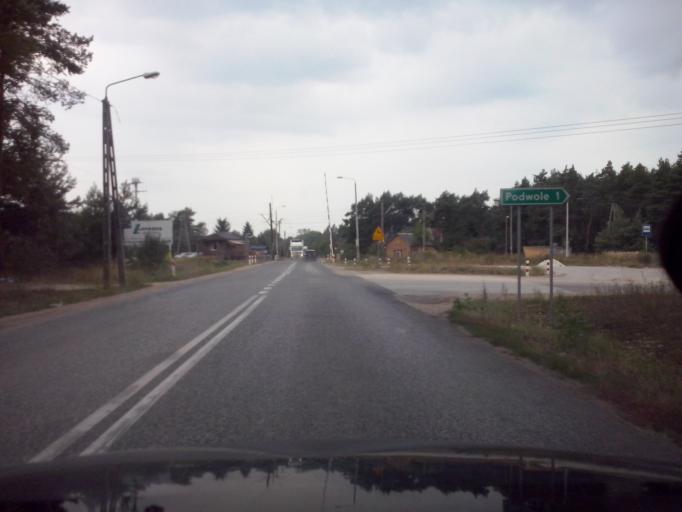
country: PL
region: Swietokrzyskie
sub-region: Kielce
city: Osiedle-Nowiny
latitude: 50.7809
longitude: 20.5307
